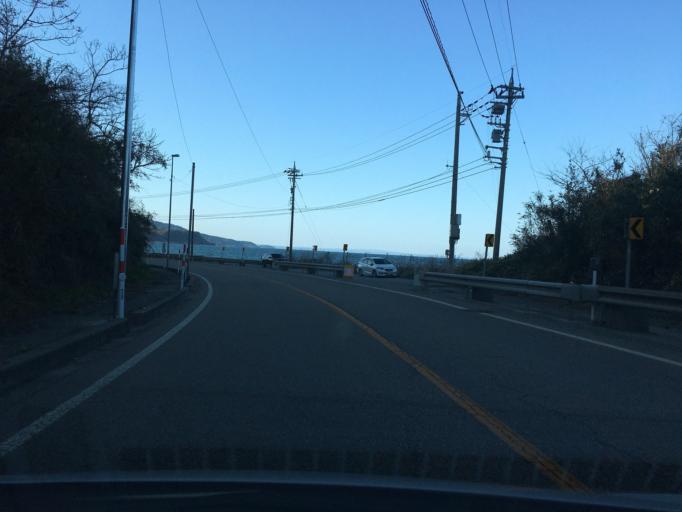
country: JP
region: Ishikawa
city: Nanao
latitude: 36.9941
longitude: 137.0533
